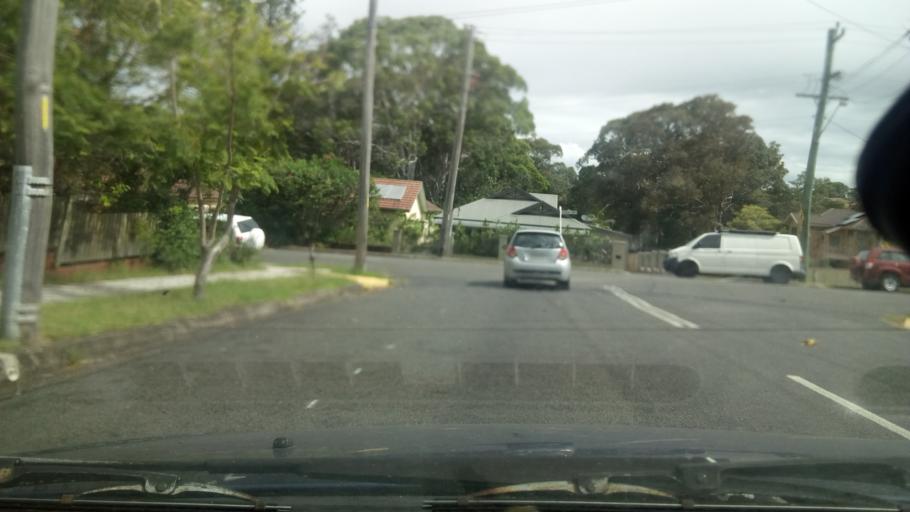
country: AU
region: New South Wales
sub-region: Wollongong
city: Gwynneville
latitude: -34.4183
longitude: 150.8807
